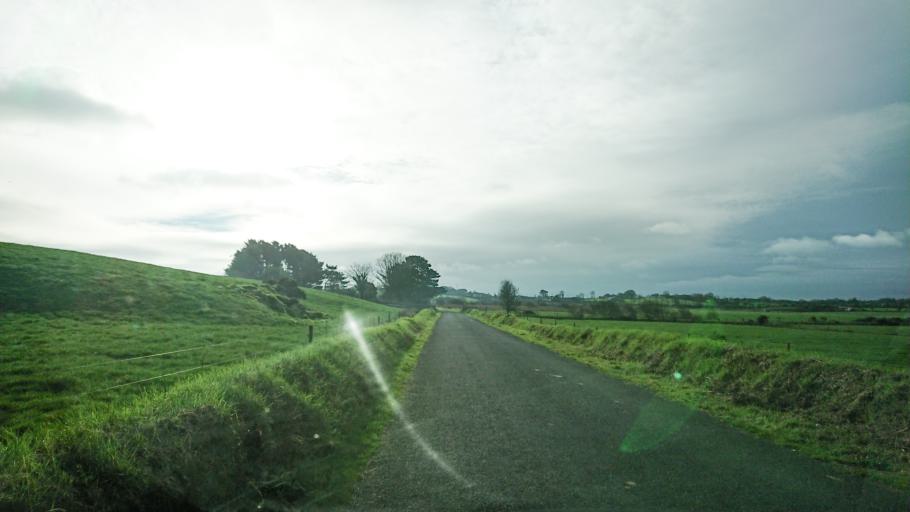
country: IE
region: Munster
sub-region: Waterford
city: Tra Mhor
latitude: 52.1635
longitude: -7.1875
